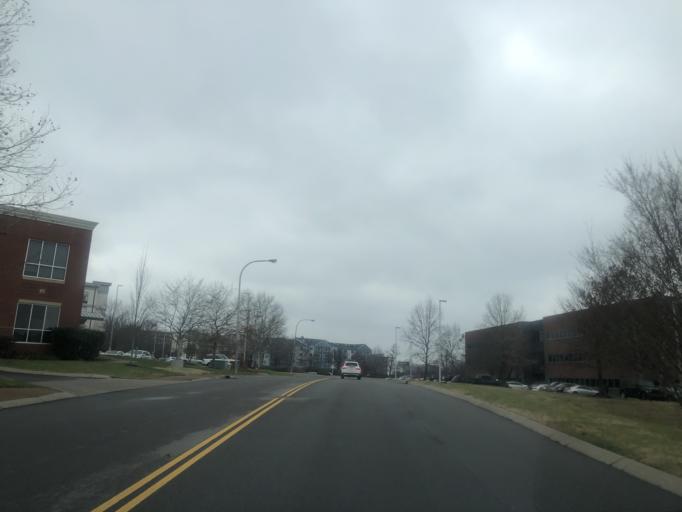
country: US
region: Tennessee
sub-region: Davidson County
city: Lakewood
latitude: 36.1447
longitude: -86.6612
